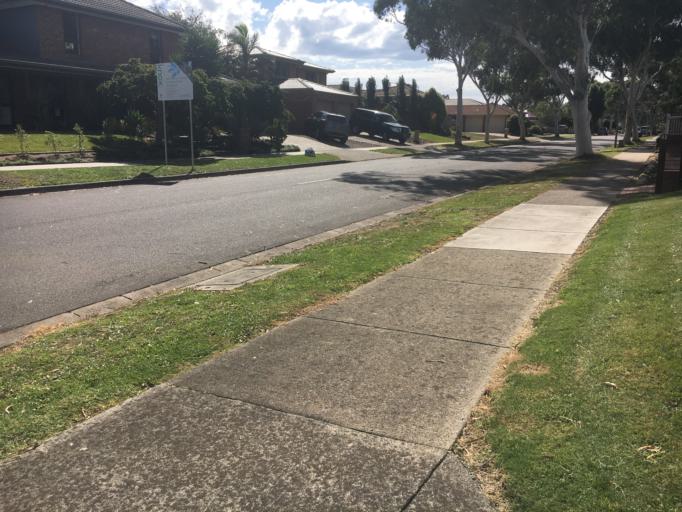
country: AU
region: Victoria
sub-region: Knox
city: Ferntree Gully
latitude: -37.8936
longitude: 145.2765
